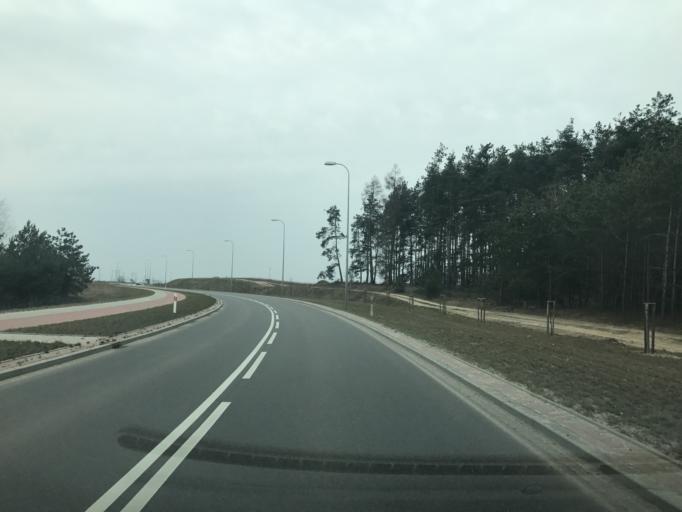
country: PL
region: Warmian-Masurian Voivodeship
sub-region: Powiat dzialdowski
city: Lidzbark
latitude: 53.2657
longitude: 19.8537
